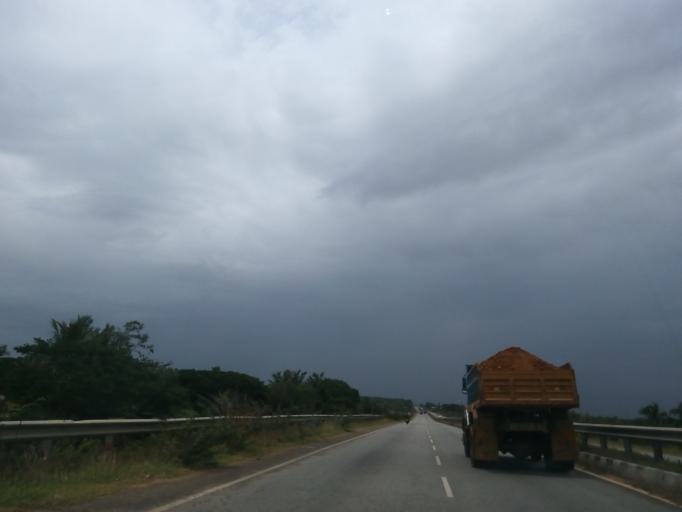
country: IN
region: Karnataka
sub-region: Davanagere
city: Harihar
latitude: 14.4690
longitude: 75.8372
